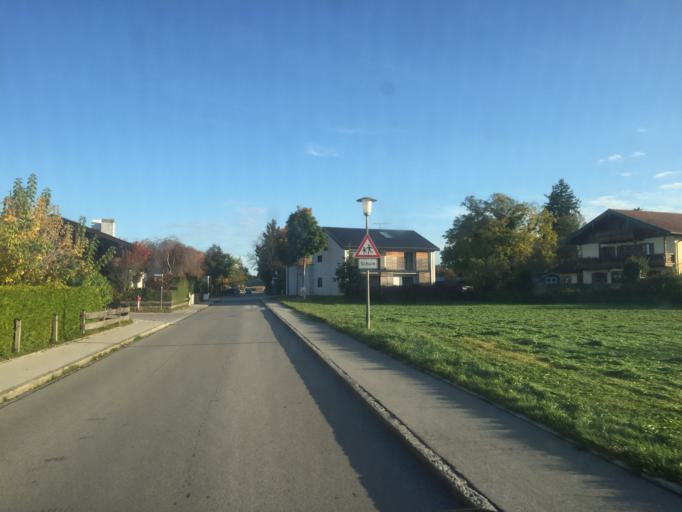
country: DE
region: Bavaria
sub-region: Upper Bavaria
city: Chieming
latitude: 47.8973
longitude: 12.5383
